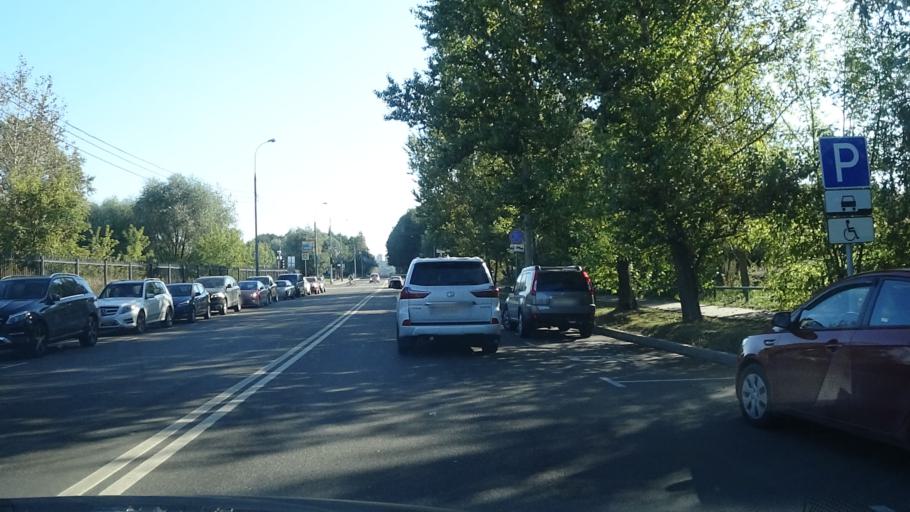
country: RU
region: Moscow
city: Shchukino
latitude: 55.7684
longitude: 37.4285
